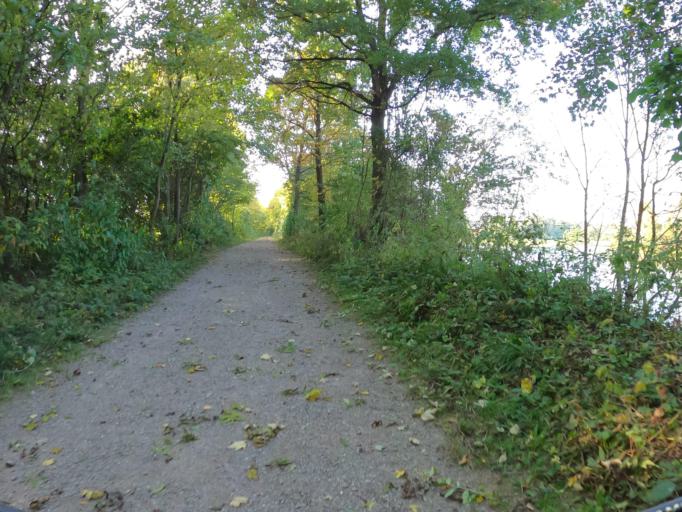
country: DE
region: Bavaria
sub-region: Swabia
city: Nersingen
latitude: 48.4452
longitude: 10.1320
